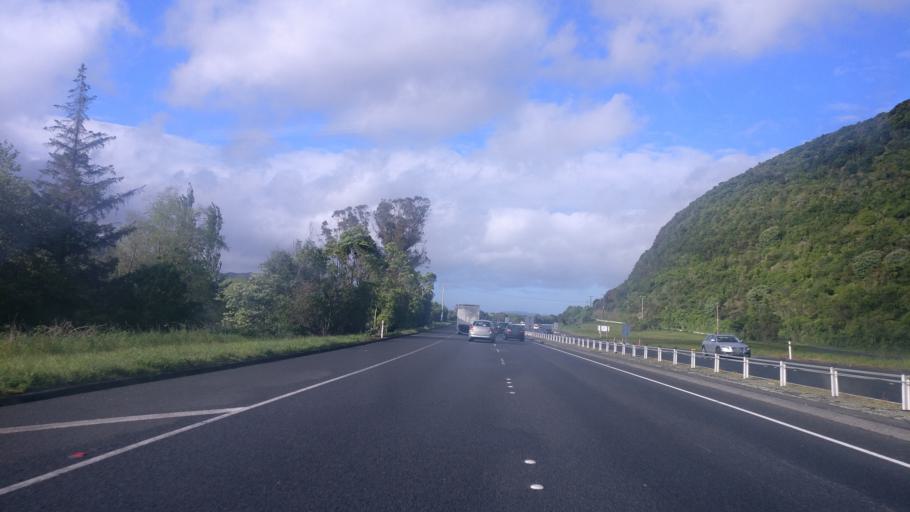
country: NZ
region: Wellington
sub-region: Lower Hutt City
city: Lower Hutt
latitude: -41.1619
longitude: 174.9686
